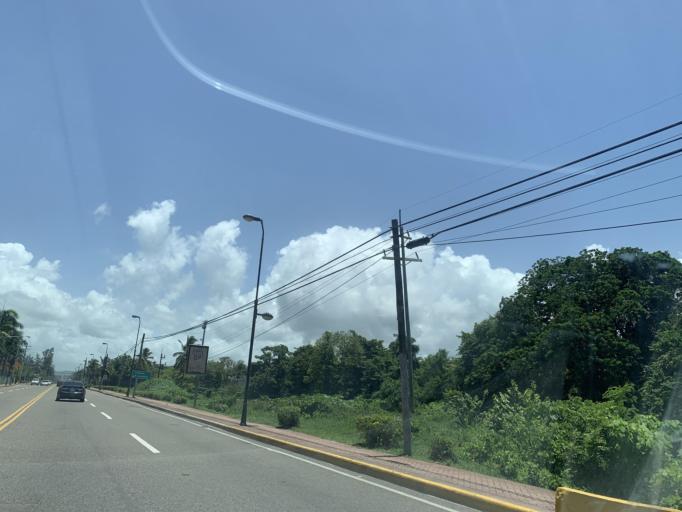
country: DO
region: Puerto Plata
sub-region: Puerto Plata
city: Puerto Plata
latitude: 19.7703
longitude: -70.6533
